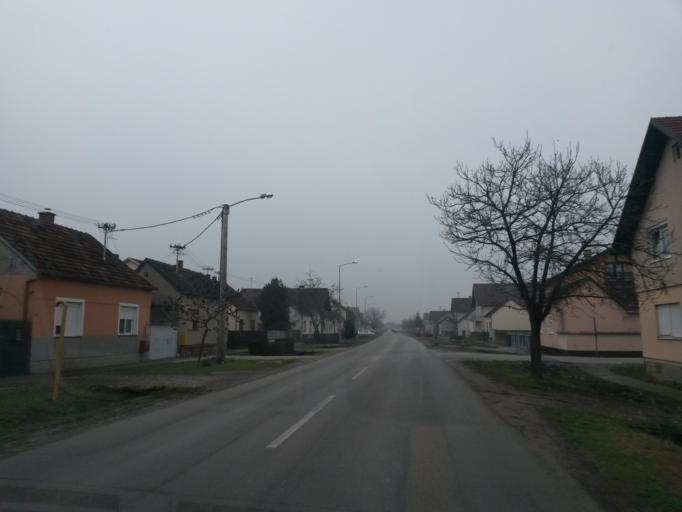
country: HR
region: Vukovarsko-Srijemska
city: Zupanja
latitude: 45.0832
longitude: 18.6984
